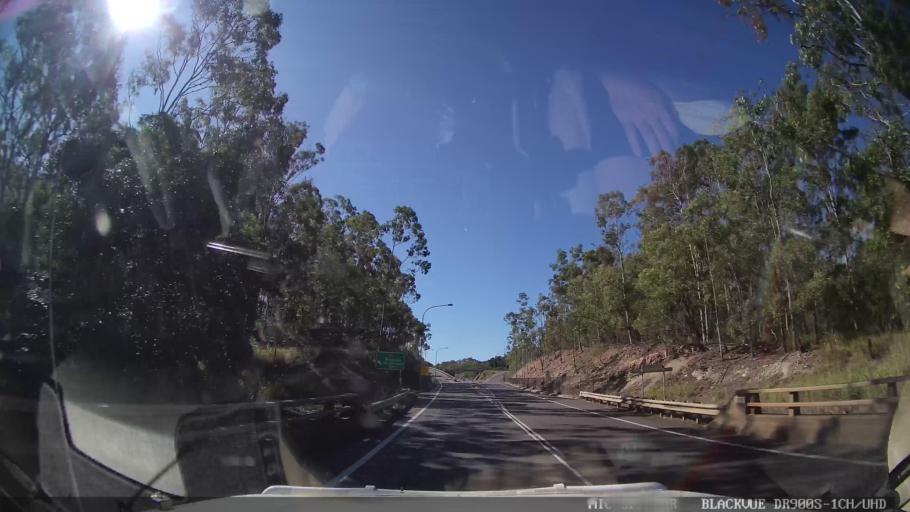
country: AU
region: Queensland
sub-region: Fraser Coast
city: Maryborough
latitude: -25.5220
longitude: 152.6669
